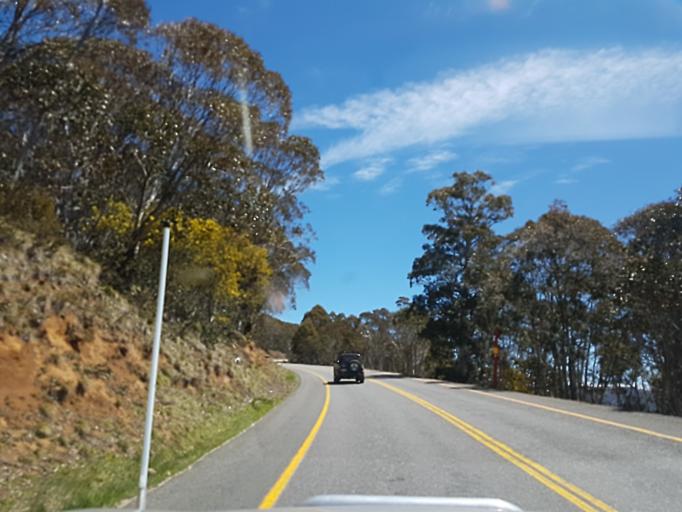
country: AU
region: Victoria
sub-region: Alpine
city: Mount Beauty
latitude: -37.0237
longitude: 147.2679
